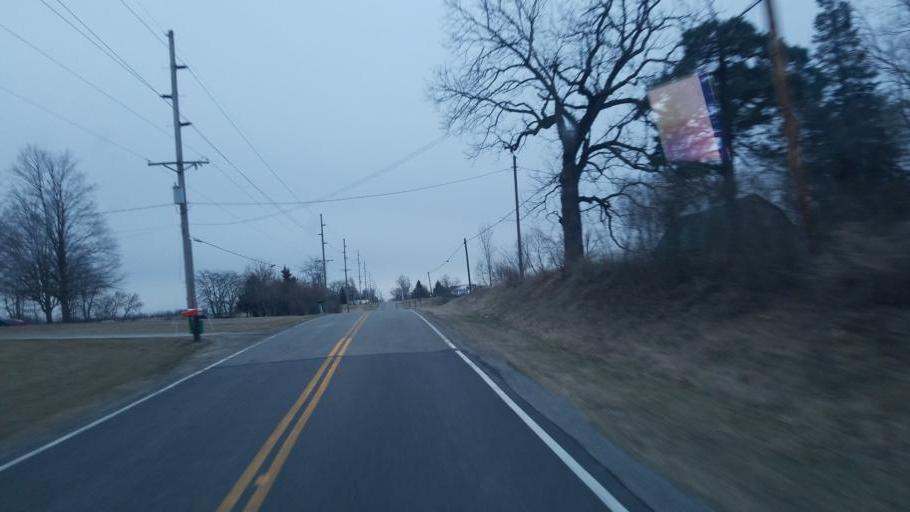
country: US
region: Ohio
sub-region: Defiance County
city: Hicksville
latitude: 41.3181
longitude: -84.7668
